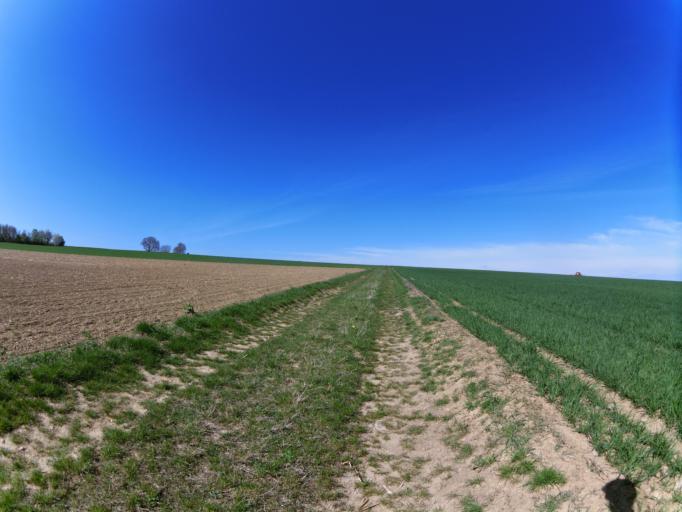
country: DE
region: Bavaria
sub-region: Regierungsbezirk Unterfranken
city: Winterhausen
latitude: 49.6821
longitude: 10.0009
